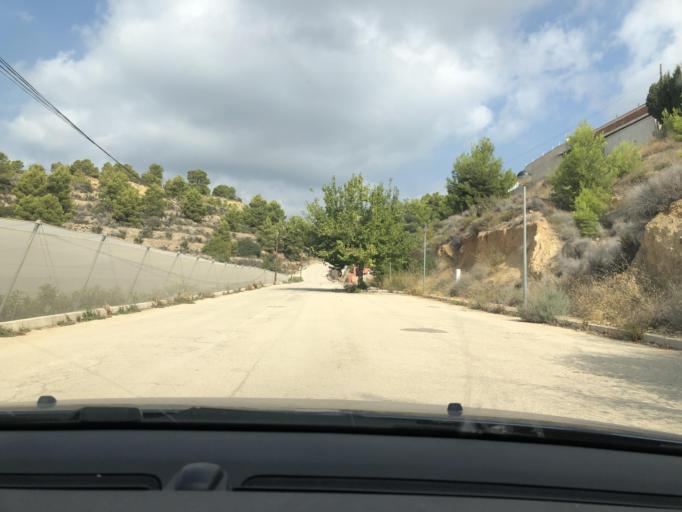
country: ES
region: Valencia
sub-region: Provincia de Alicante
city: Callosa d'En Sarria
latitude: 38.6337
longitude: -0.1124
